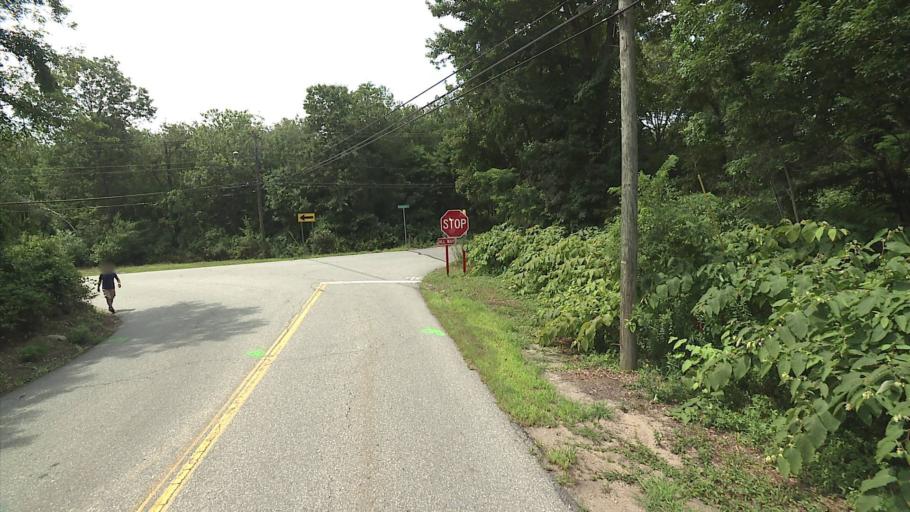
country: US
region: Connecticut
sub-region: New London County
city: Central Waterford
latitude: 41.3099
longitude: -72.1136
